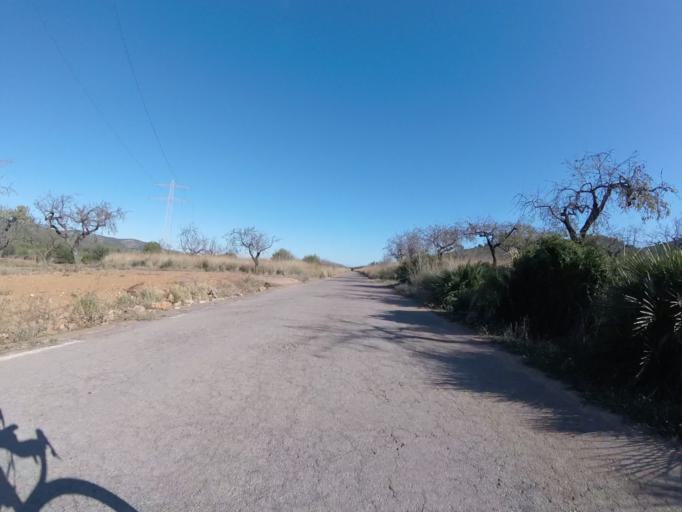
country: ES
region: Valencia
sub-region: Provincia de Castello
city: Orpesa/Oropesa del Mar
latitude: 40.1241
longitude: 0.1134
